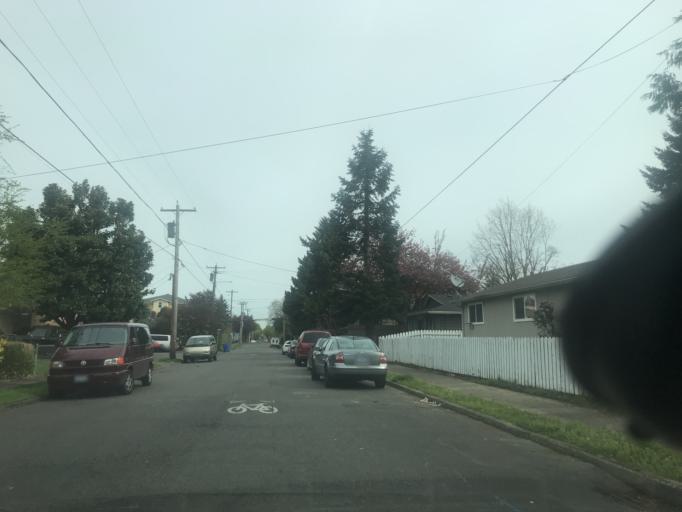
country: US
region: Oregon
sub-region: Multnomah County
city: Lents
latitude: 45.4928
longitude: -122.5810
